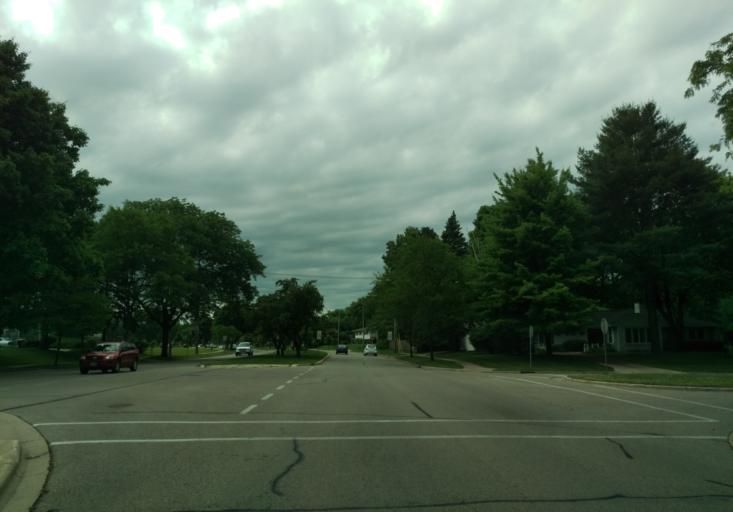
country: US
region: Wisconsin
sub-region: Dane County
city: Shorewood Hills
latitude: 43.0361
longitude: -89.4778
